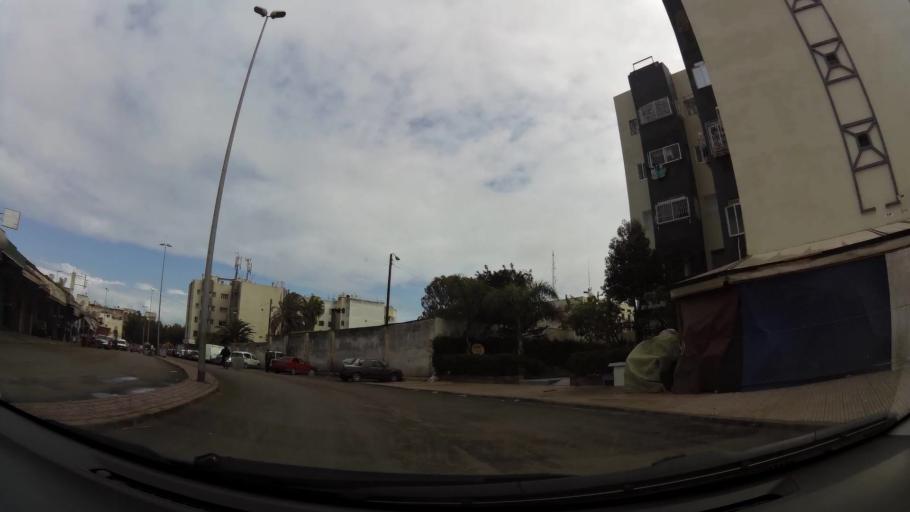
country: MA
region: Grand Casablanca
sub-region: Casablanca
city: Casablanca
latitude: 33.5683
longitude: -7.6728
